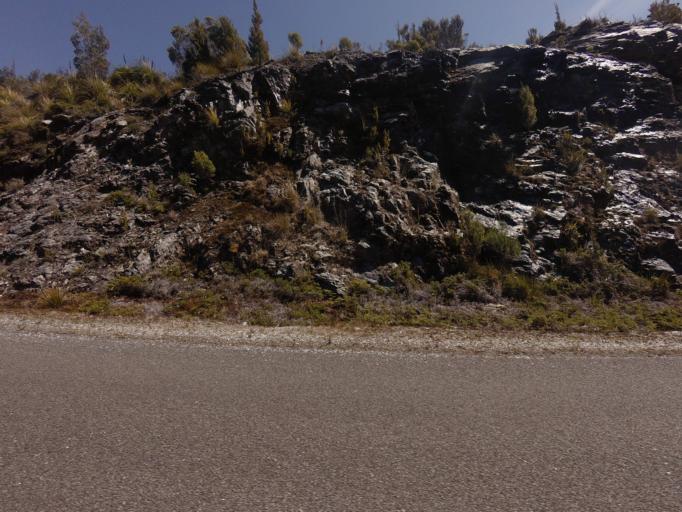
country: AU
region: Tasmania
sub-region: West Coast
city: Queenstown
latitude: -42.7508
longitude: 145.9816
